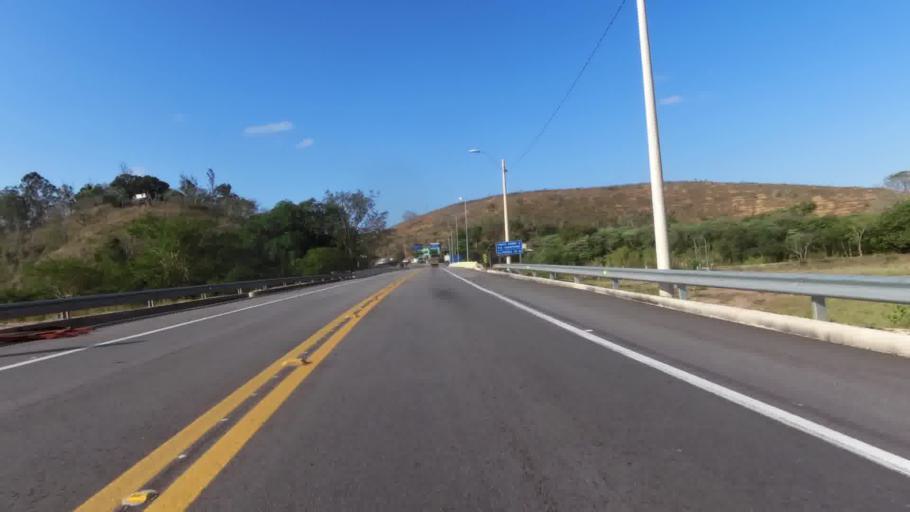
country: BR
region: Espirito Santo
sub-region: Mimoso Do Sul
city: Mimoso do Sul
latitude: -21.2228
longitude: -41.3097
